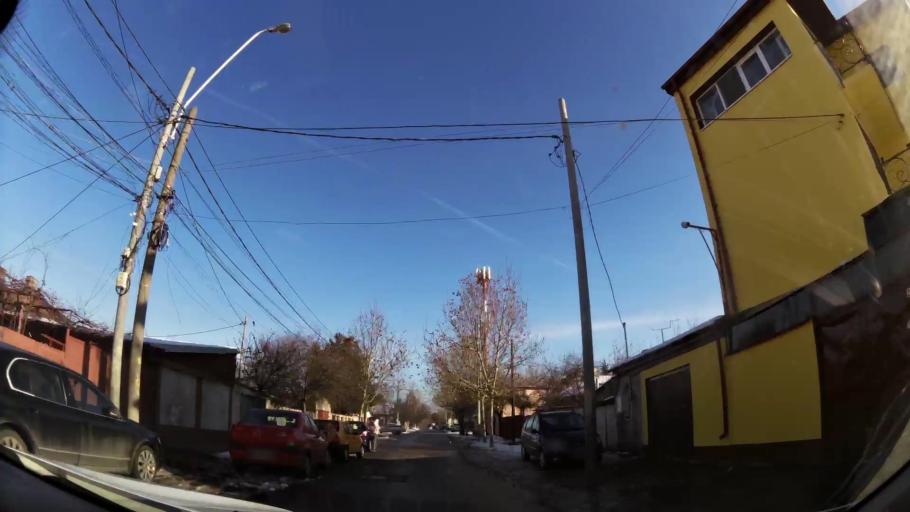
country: RO
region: Ilfov
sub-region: Voluntari City
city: Voluntari
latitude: 44.4815
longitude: 26.1488
